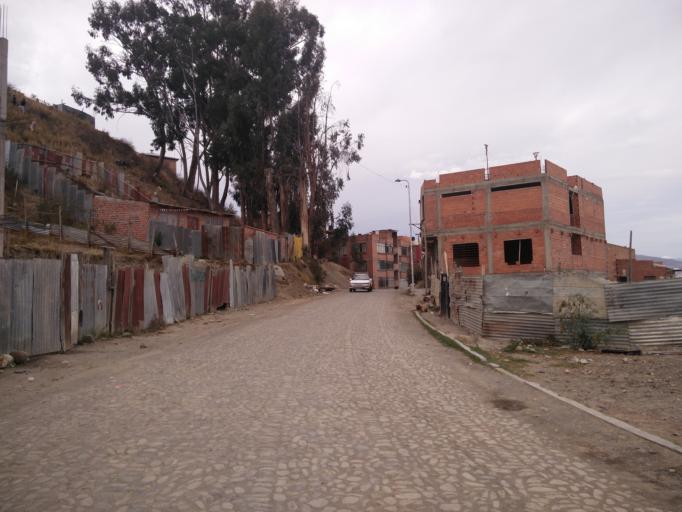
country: BO
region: La Paz
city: La Paz
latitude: -16.5198
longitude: -68.1291
